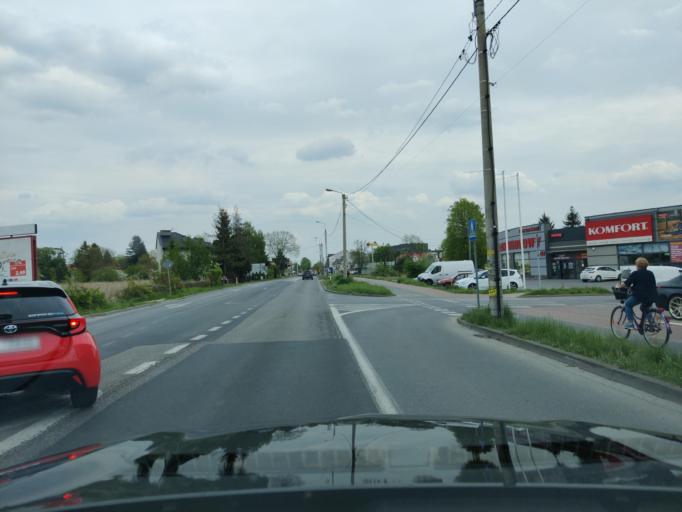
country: PL
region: Masovian Voivodeship
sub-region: Powiat wyszkowski
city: Wyszkow
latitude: 52.5988
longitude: 21.4412
